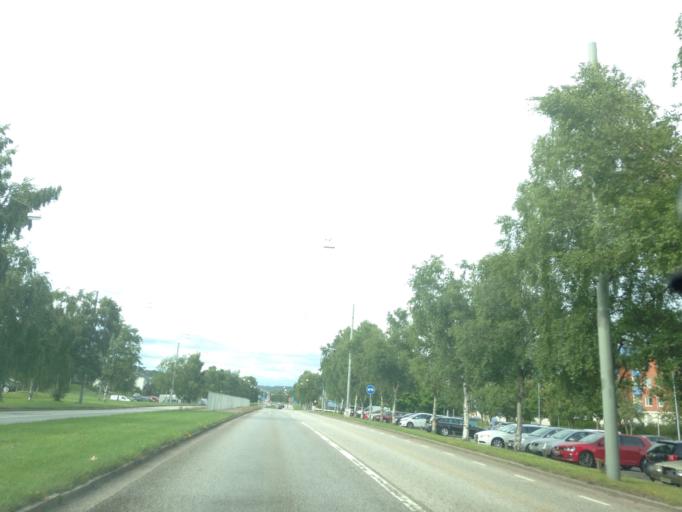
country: SE
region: Vaestra Goetaland
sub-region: Goteborg
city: Goeteborg
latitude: 57.7444
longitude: 11.9761
